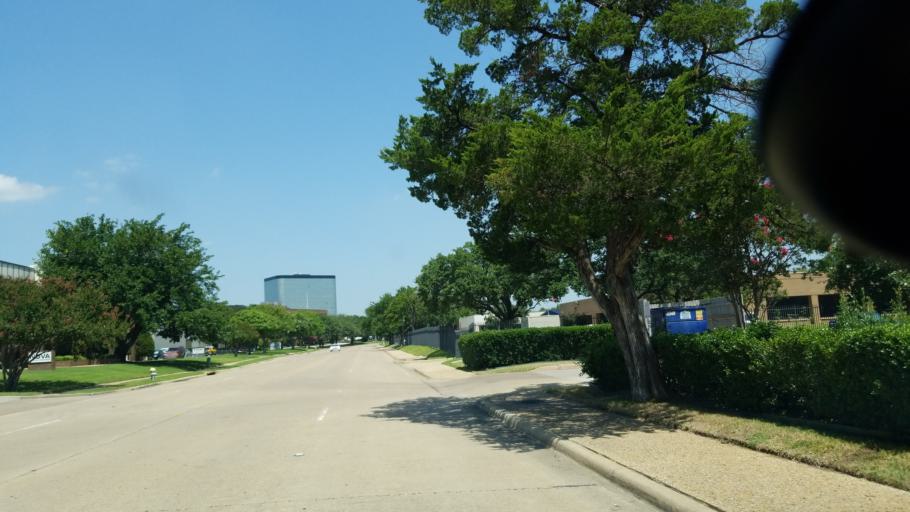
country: US
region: Texas
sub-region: Dallas County
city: University Park
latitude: 32.8237
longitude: -96.8647
